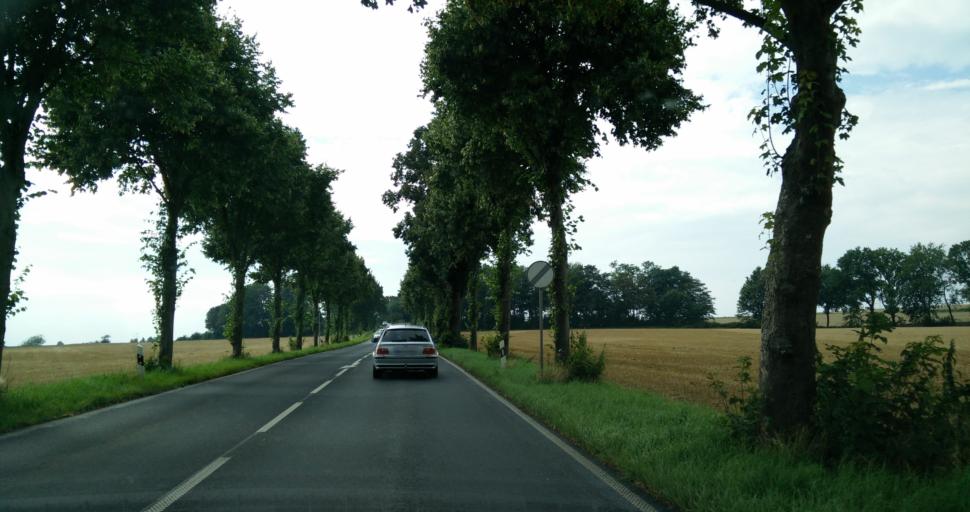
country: DE
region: North Rhine-Westphalia
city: Wulfrath
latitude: 51.2494
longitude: 7.0308
